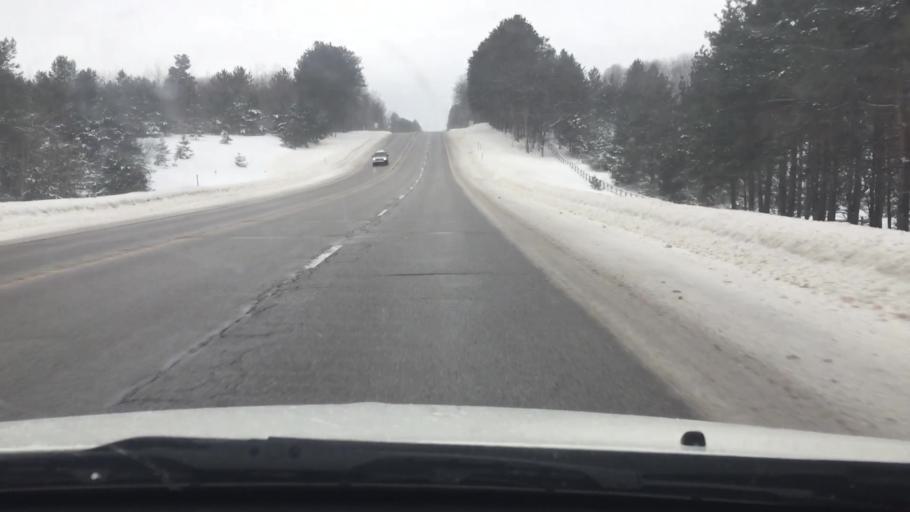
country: US
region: Michigan
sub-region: Otsego County
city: Gaylord
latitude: 45.0621
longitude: -84.8230
